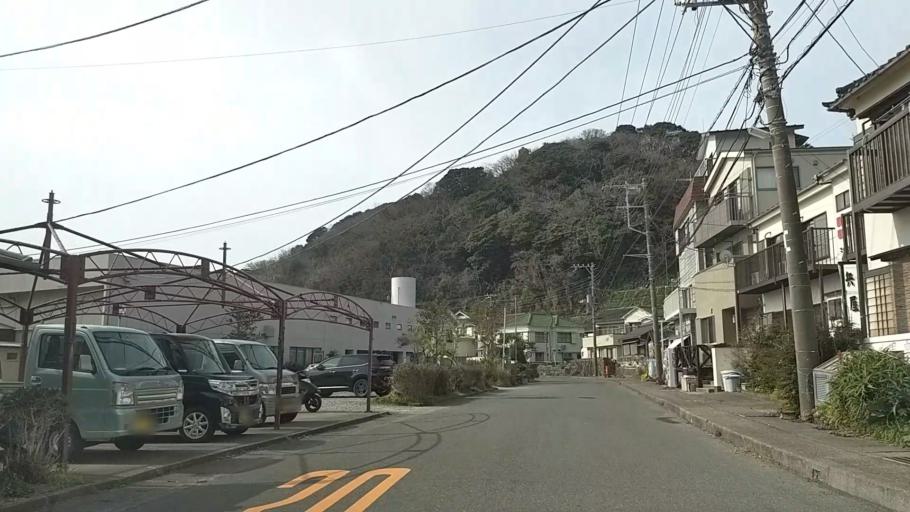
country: JP
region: Shizuoka
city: Shimoda
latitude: 34.6569
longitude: 138.9670
